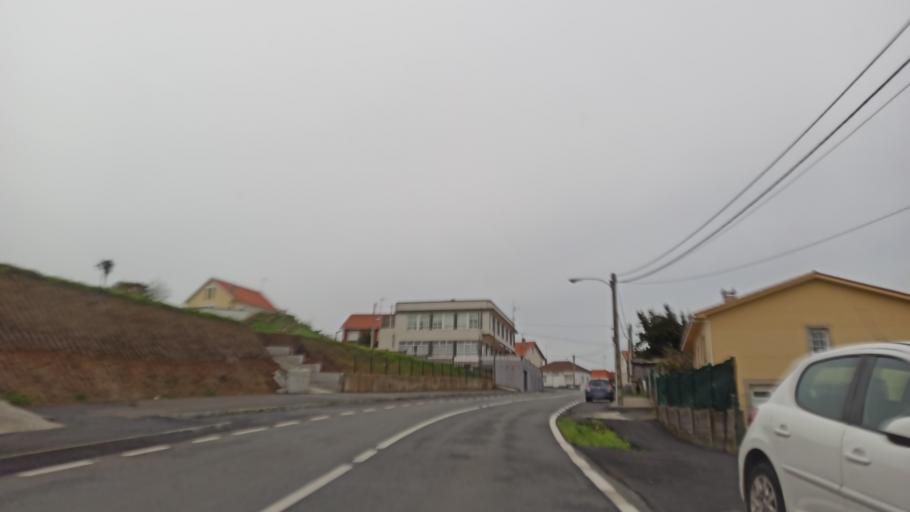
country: ES
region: Galicia
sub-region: Provincia da Coruna
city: Oleiros
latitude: 43.3896
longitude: -8.3061
